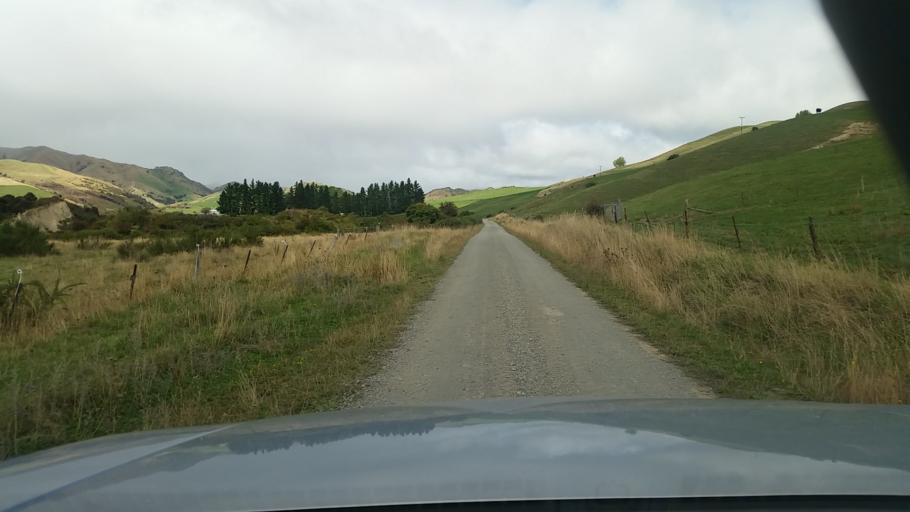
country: NZ
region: Marlborough
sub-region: Marlborough District
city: Blenheim
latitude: -41.7390
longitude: 173.8932
